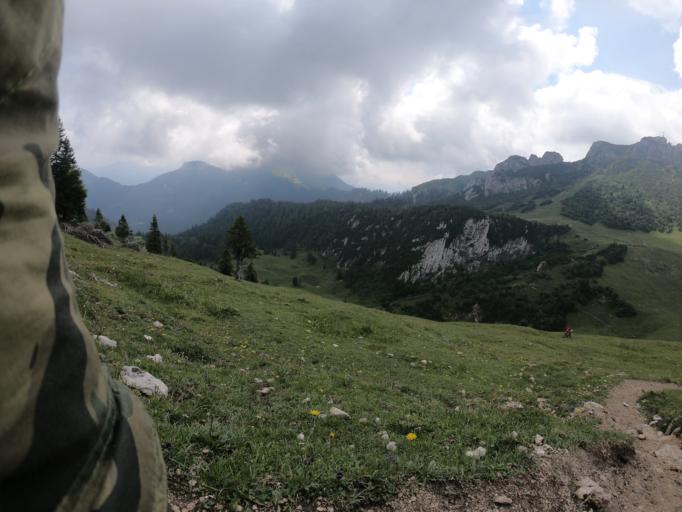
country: DE
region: Bavaria
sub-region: Upper Bavaria
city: Aschau im Chiemgau
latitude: 47.7626
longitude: 12.3679
